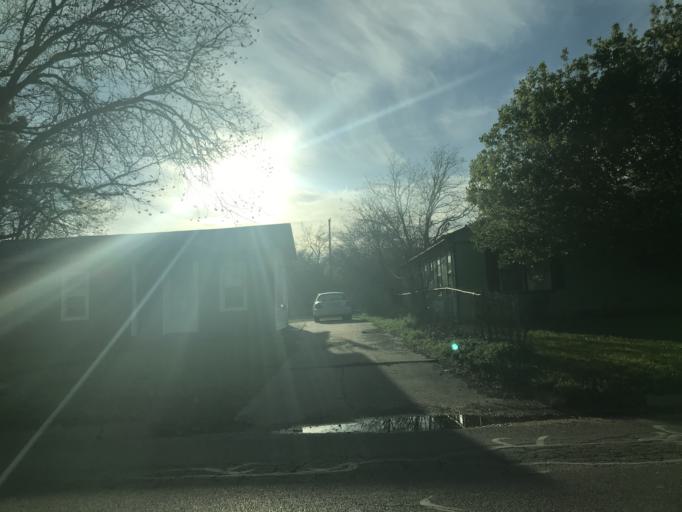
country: US
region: Texas
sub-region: Taylor County
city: Abilene
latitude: 32.4353
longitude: -99.7641
